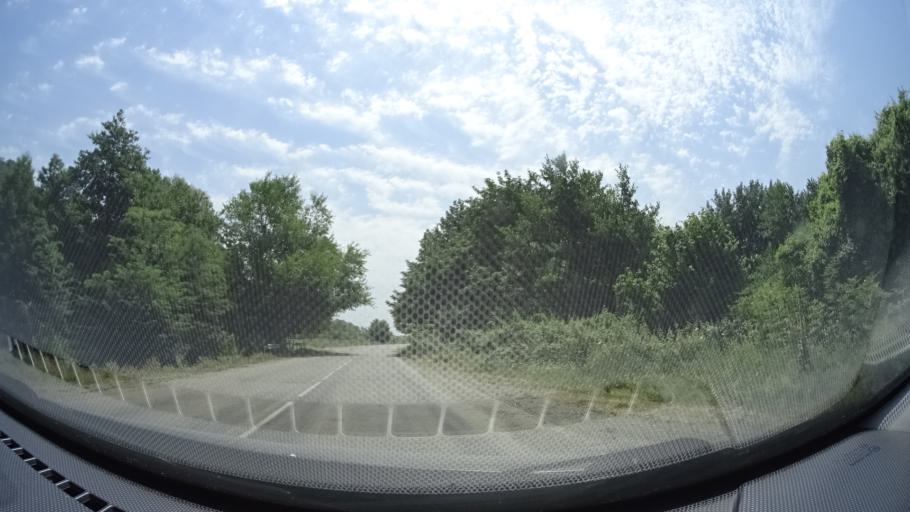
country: GE
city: Bagdadi
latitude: 41.8581
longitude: 46.0265
